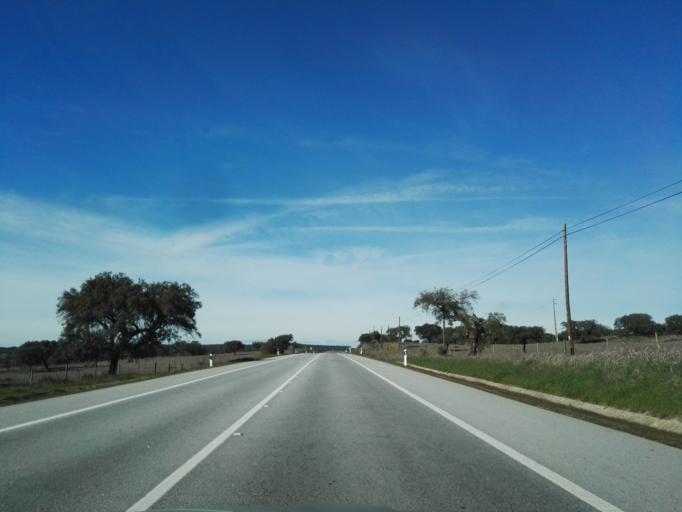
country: PT
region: Portalegre
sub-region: Arronches
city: Arronches
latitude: 39.1499
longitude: -7.3096
